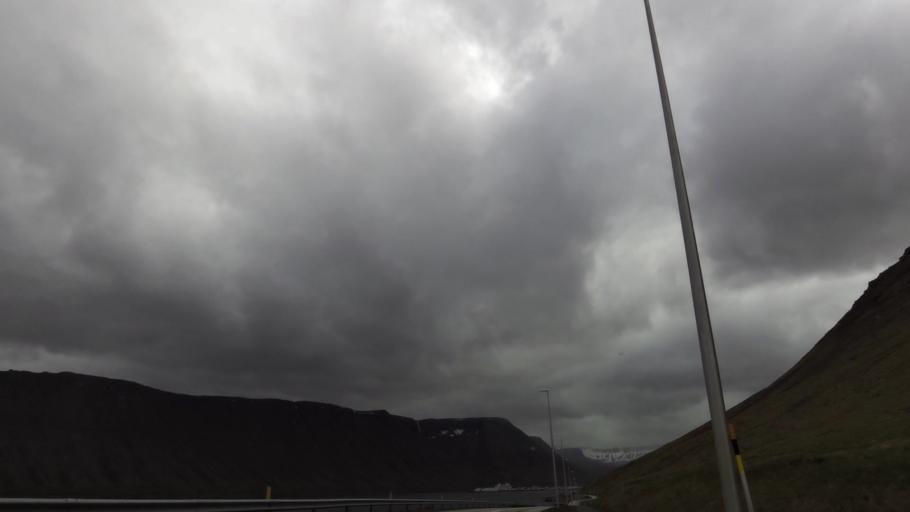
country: IS
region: Westfjords
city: Isafjoerdur
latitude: 66.0999
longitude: -23.1094
